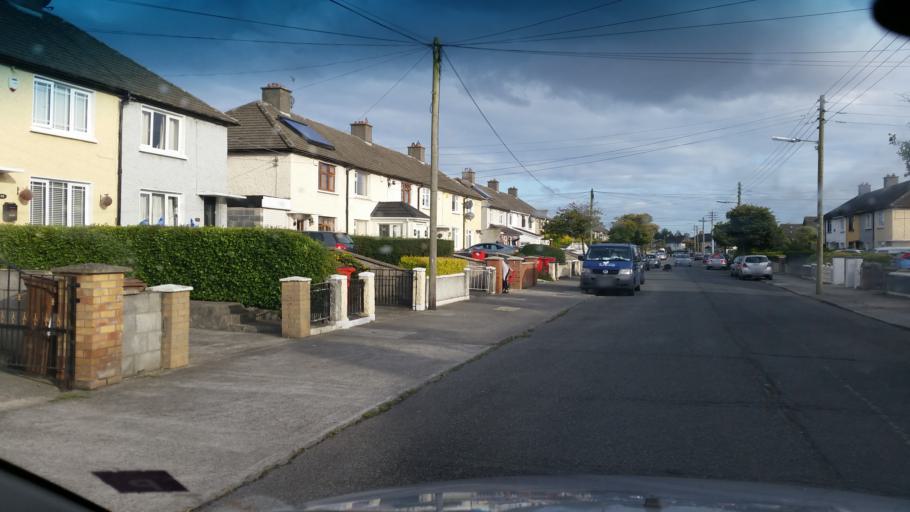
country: IE
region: Leinster
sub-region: Dublin City
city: Finglas
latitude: 53.3868
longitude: -6.2922
